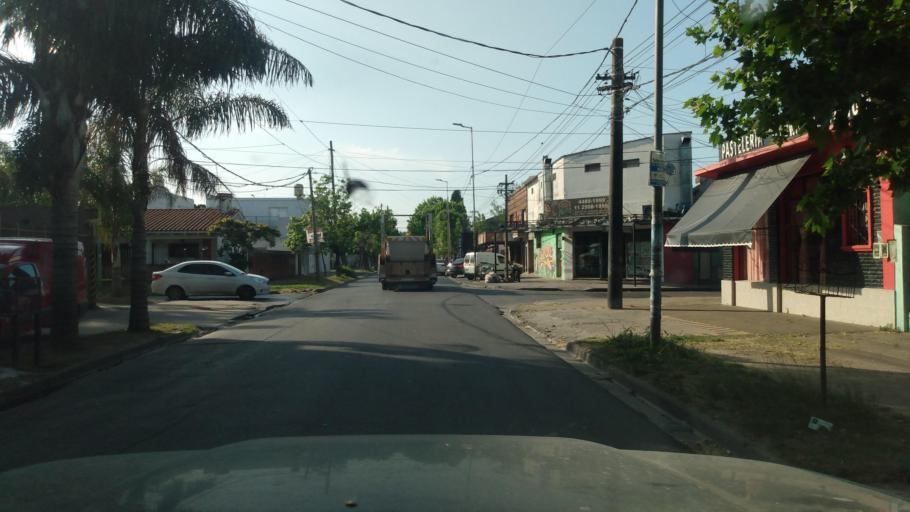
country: AR
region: Buenos Aires
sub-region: Partido de Moron
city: Moron
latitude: -34.6430
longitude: -58.6138
